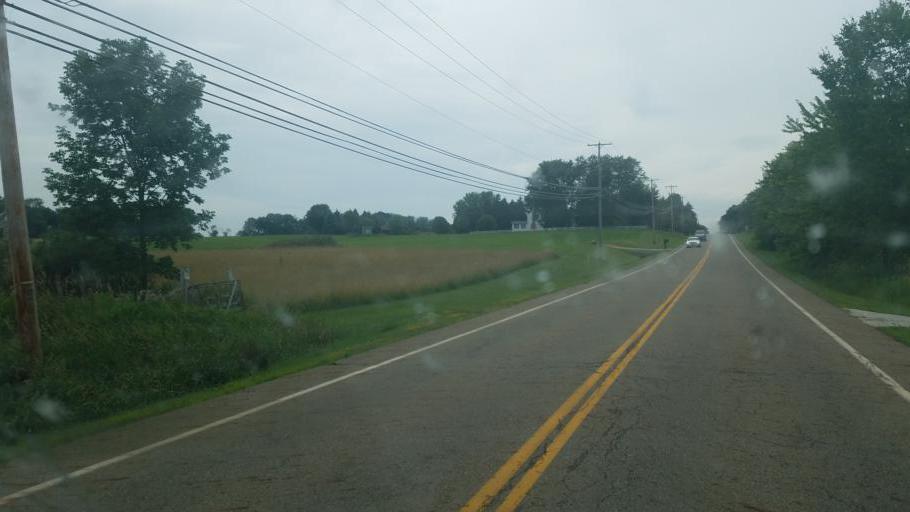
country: US
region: Ohio
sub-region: Summit County
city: Manchester
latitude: 40.9318
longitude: -81.5967
